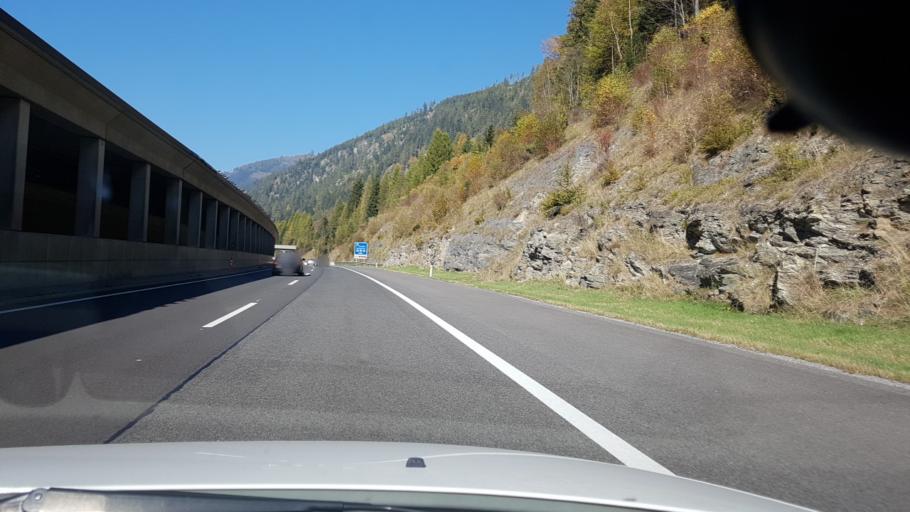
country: AT
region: Salzburg
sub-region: Politischer Bezirk Tamsweg
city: Sankt Michael im Lungau
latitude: 47.1036
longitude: 13.5982
